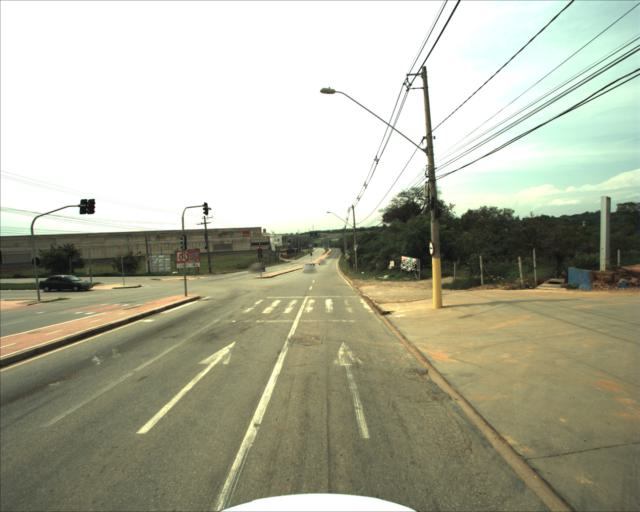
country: BR
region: Sao Paulo
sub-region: Sorocaba
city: Sorocaba
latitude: -23.4342
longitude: -47.4366
